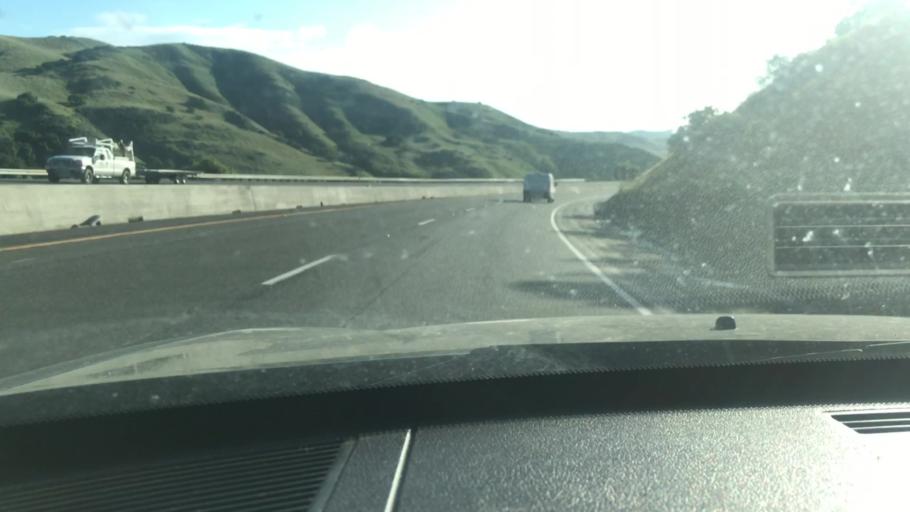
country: US
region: California
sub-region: Merced County
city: Gustine
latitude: 37.0765
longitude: -121.2081
